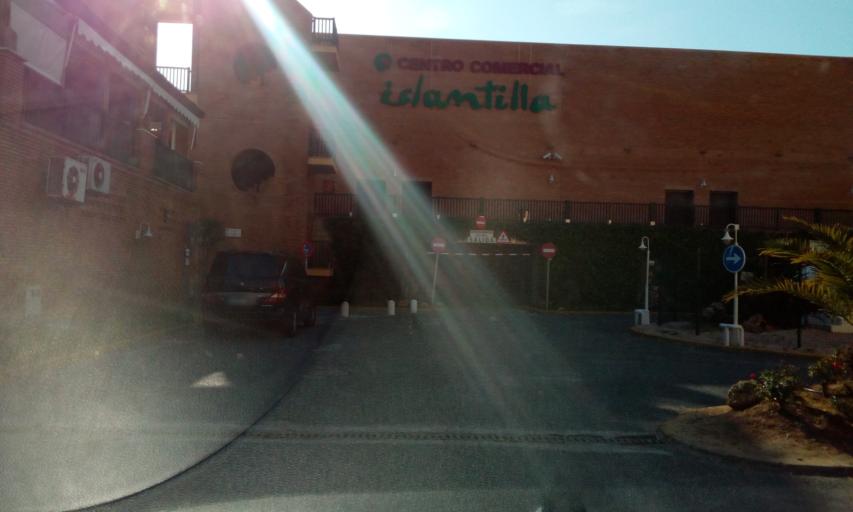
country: ES
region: Andalusia
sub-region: Provincia de Huelva
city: Lepe
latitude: 37.2054
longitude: -7.2369
